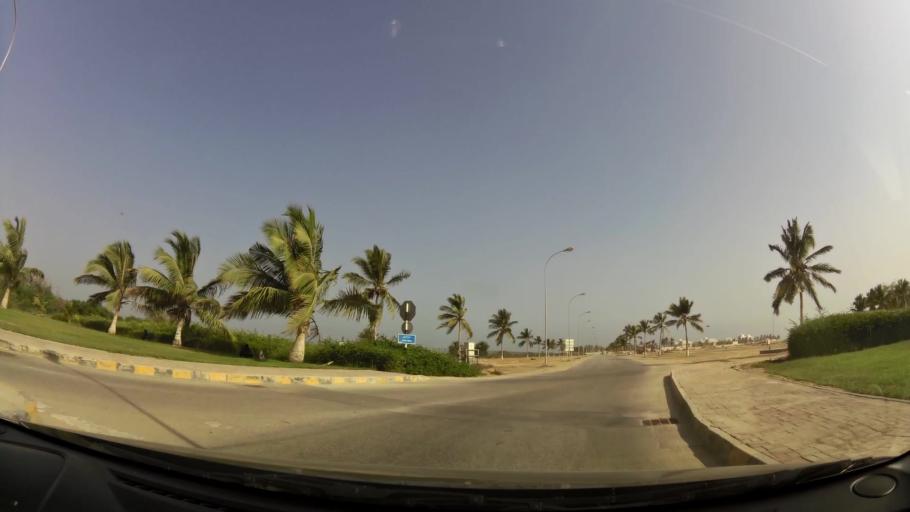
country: OM
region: Zufar
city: Salalah
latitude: 17.0023
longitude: 54.0657
